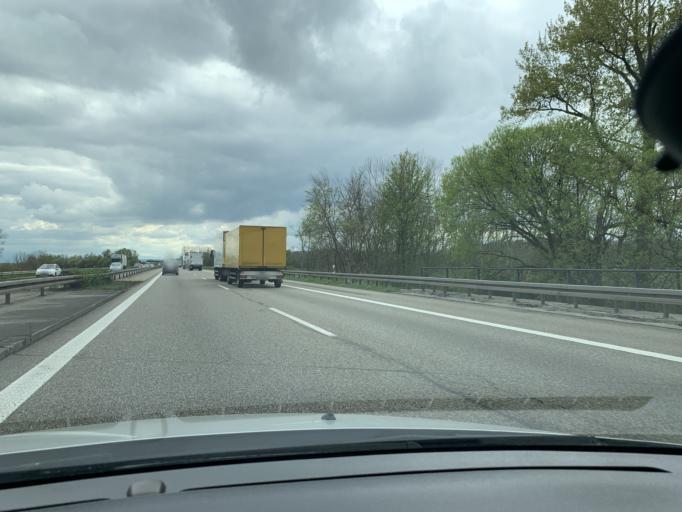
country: DE
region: Baden-Wuerttemberg
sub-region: Freiburg Region
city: Kenzingen
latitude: 48.2112
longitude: 7.7461
